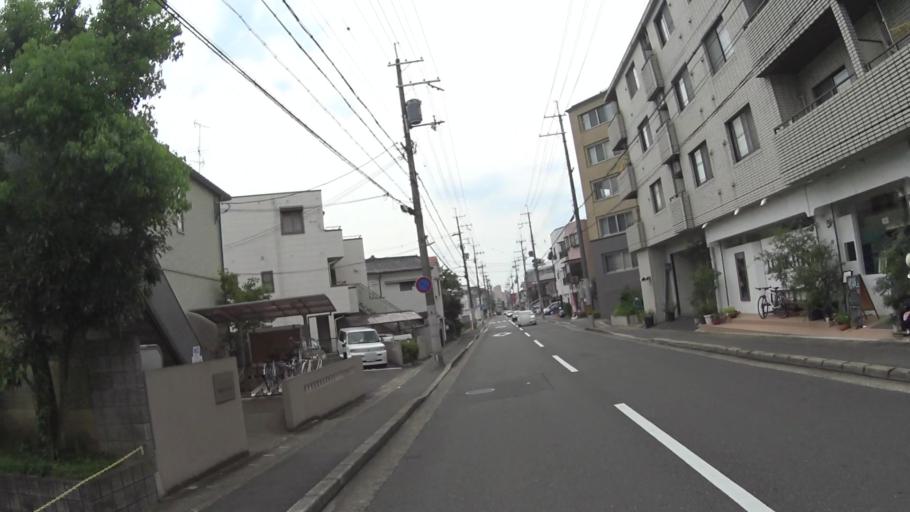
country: JP
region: Kyoto
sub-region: Kyoto-shi
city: Kamigyo-ku
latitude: 35.0497
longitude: 135.7895
